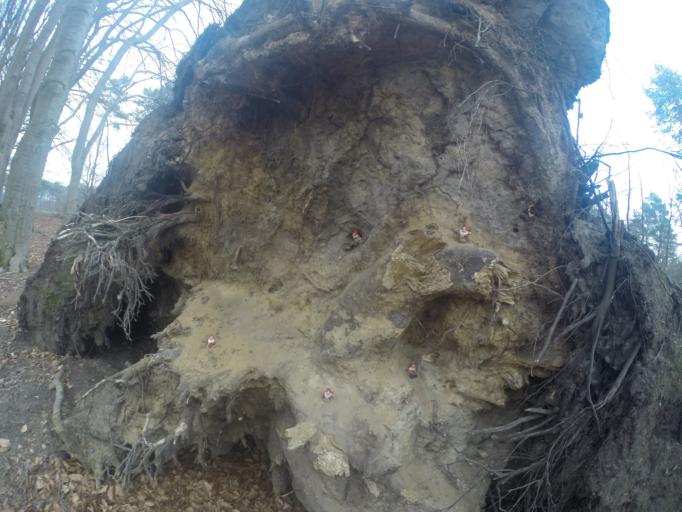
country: NL
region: Gelderland
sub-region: Gemeente Lochem
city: Almen
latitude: 52.1316
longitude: 6.2826
